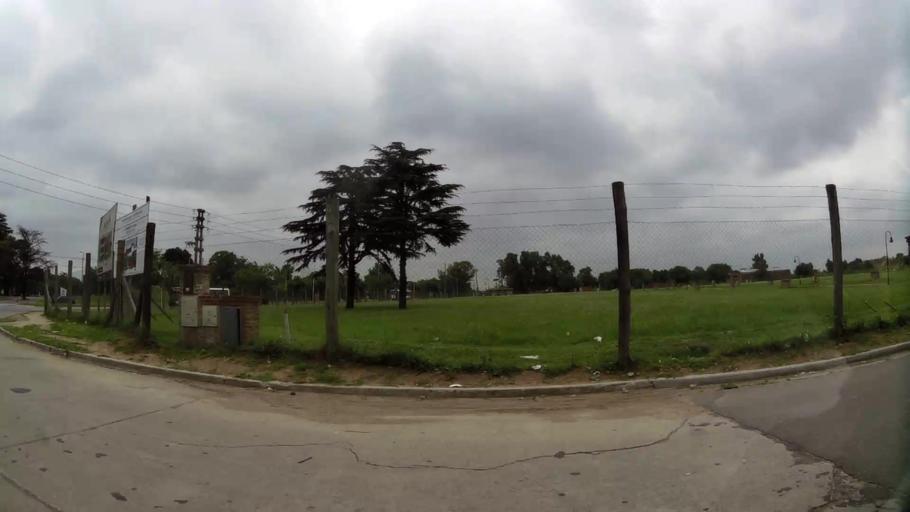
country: AR
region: Buenos Aires
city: San Justo
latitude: -34.7315
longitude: -58.5228
